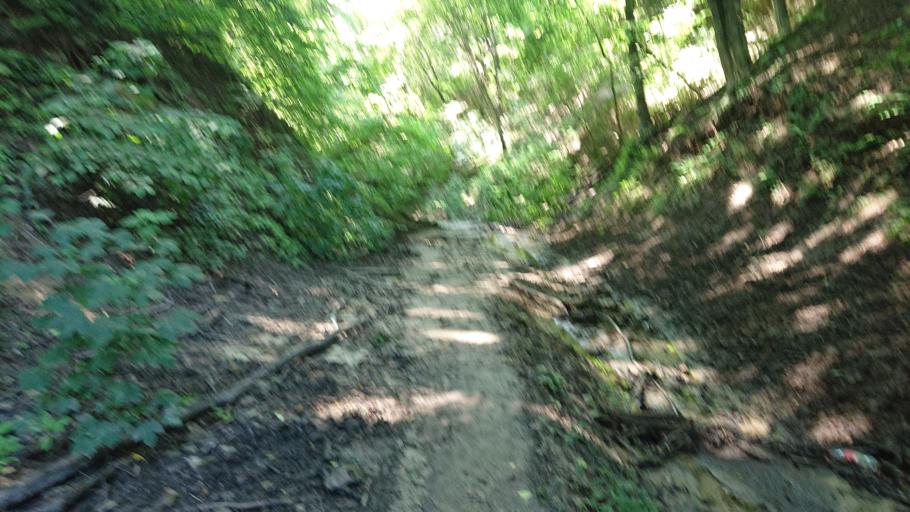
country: PL
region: Lublin Voivodeship
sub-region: Powiat pulawski
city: Kazimierz Dolny
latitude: 51.3272
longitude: 21.9643
